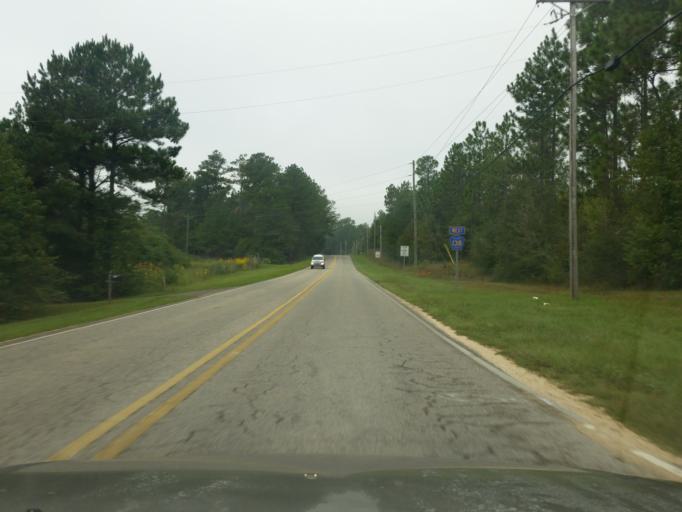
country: US
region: Alabama
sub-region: Baldwin County
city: Bay Minette
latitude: 30.8519
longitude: -87.8141
